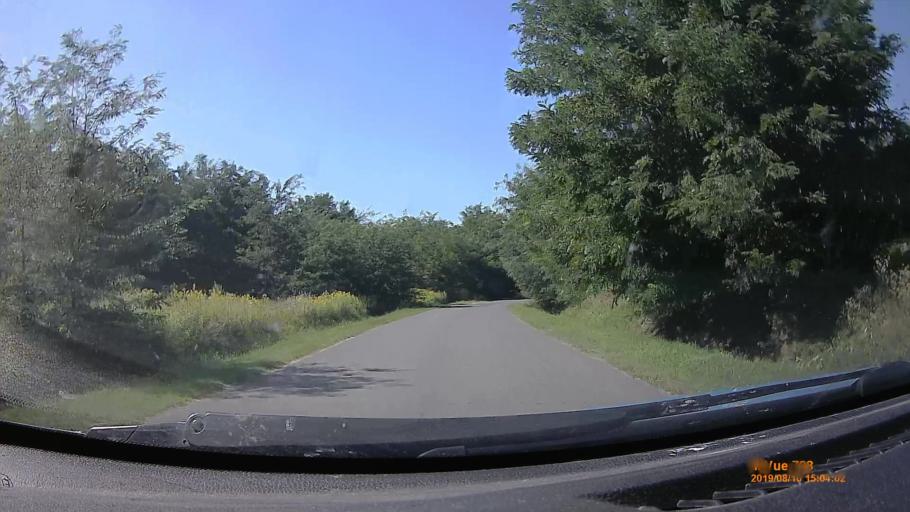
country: HU
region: Somogy
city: Lengyeltoti
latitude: 46.6714
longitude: 17.5686
